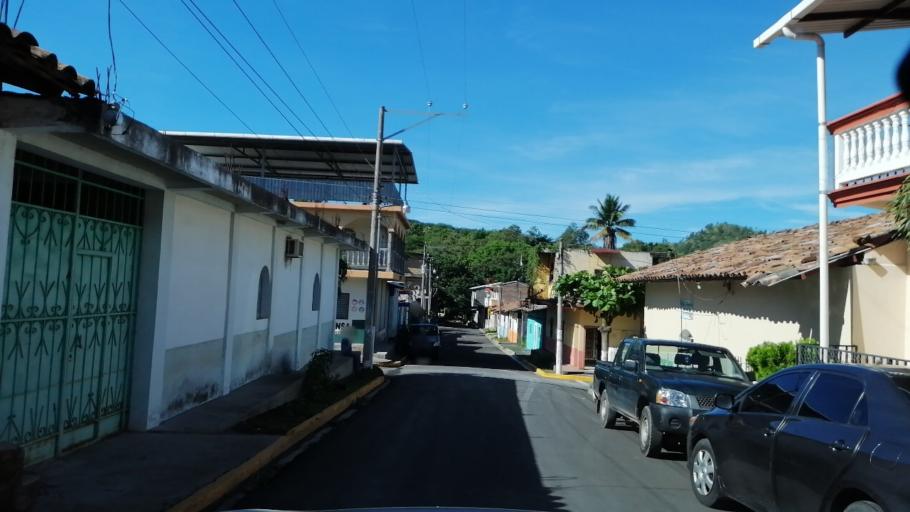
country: SV
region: Morazan
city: Corinto
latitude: 13.8085
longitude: -87.9706
